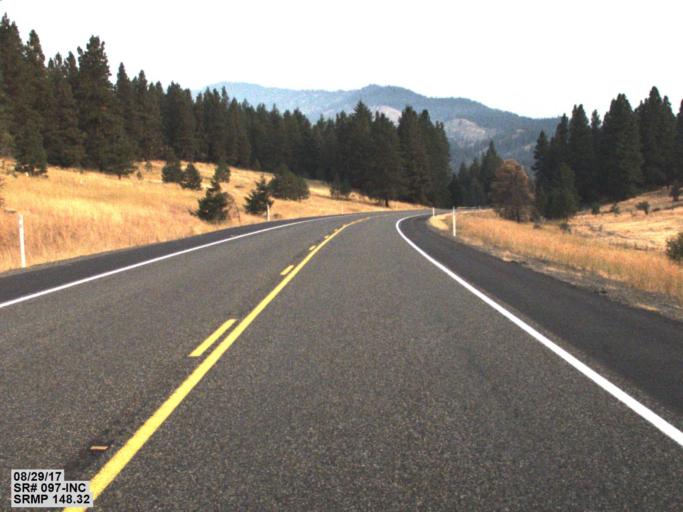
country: US
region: Washington
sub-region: Kittitas County
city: Cle Elum
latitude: 47.1839
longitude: -120.7067
